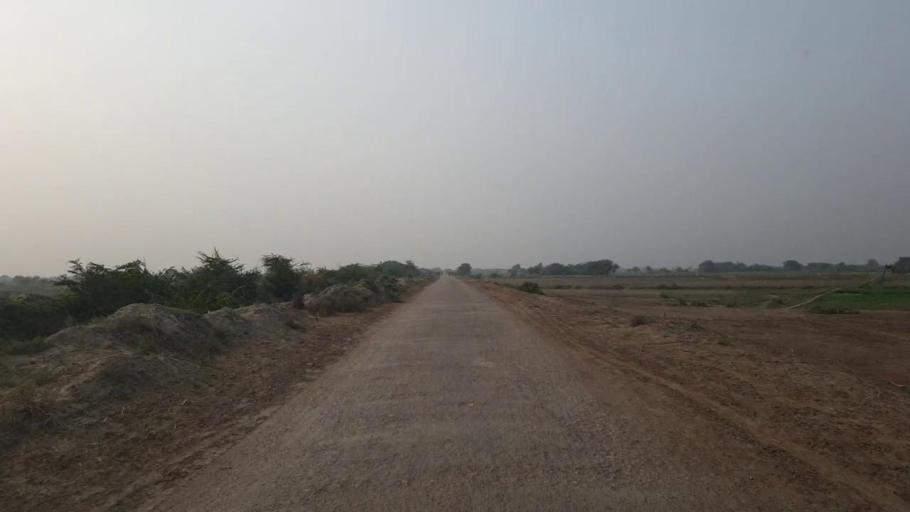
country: PK
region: Sindh
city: Mirpur Batoro
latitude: 24.6430
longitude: 68.3952
